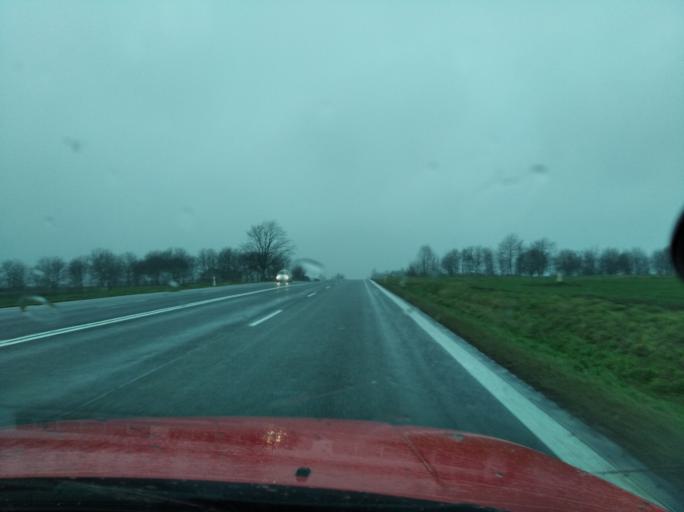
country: PL
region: Subcarpathian Voivodeship
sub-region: Powiat przeworski
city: Nowosielce
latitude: 50.0659
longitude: 22.4047
